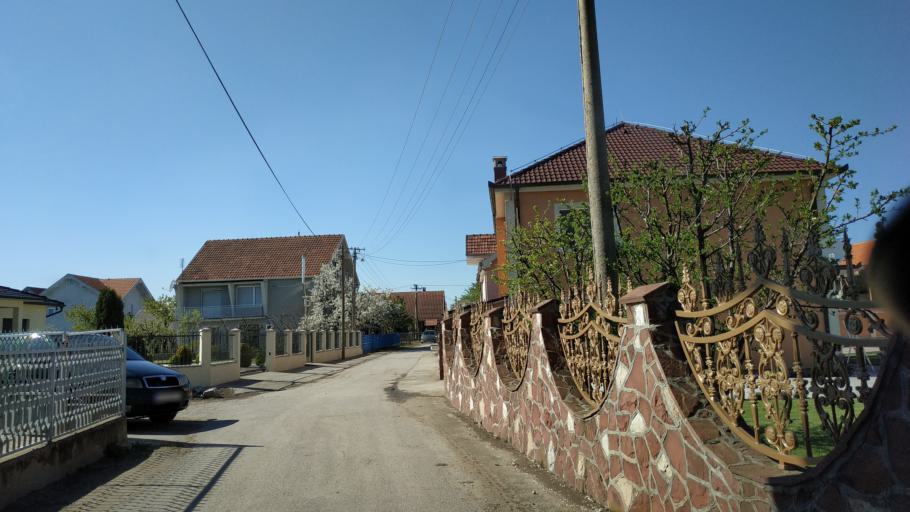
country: RS
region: Central Serbia
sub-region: Nisavski Okrug
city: Aleksinac
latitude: 43.4977
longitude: 21.6946
